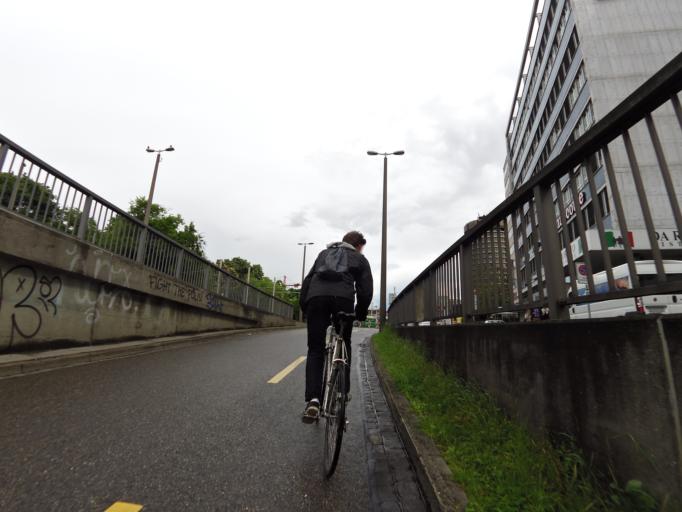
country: CH
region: Basel-City
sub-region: Basel-Stadt
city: Basel
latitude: 47.5493
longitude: 7.5892
